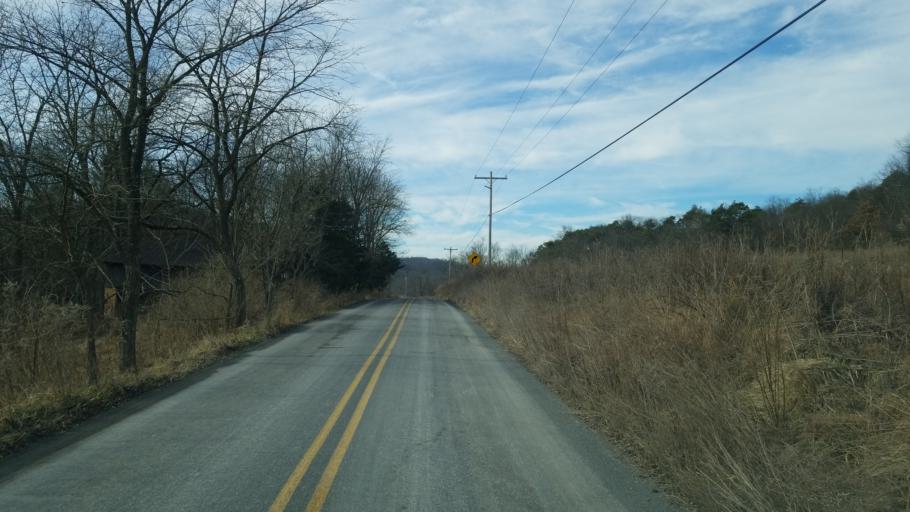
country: US
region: Pennsylvania
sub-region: Jefferson County
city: Punxsutawney
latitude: 40.8441
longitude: -79.1365
